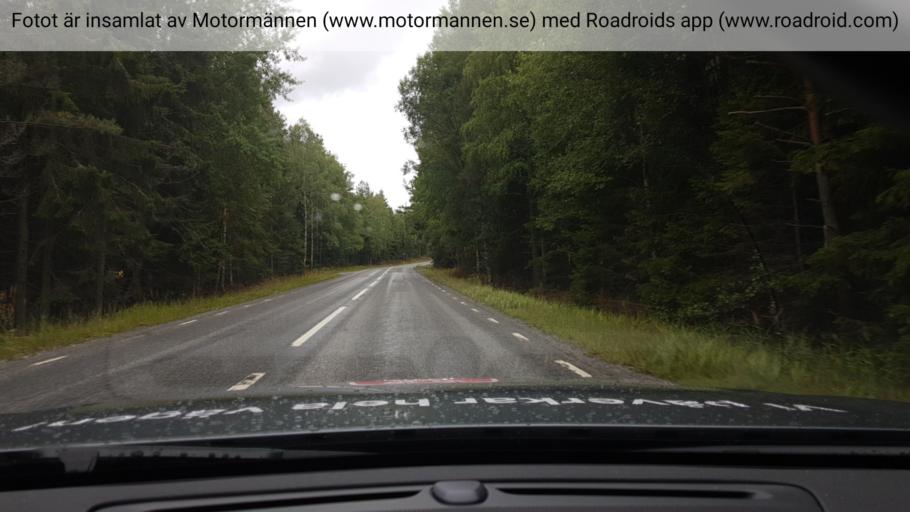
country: SE
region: Stockholm
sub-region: Botkyrka Kommun
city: Tullinge
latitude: 59.1391
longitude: 17.9291
